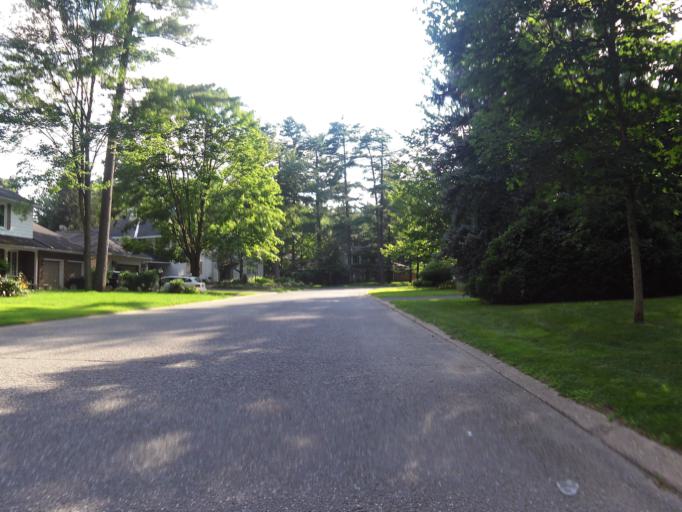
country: CA
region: Ontario
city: Bells Corners
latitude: 45.3226
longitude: -75.7898
